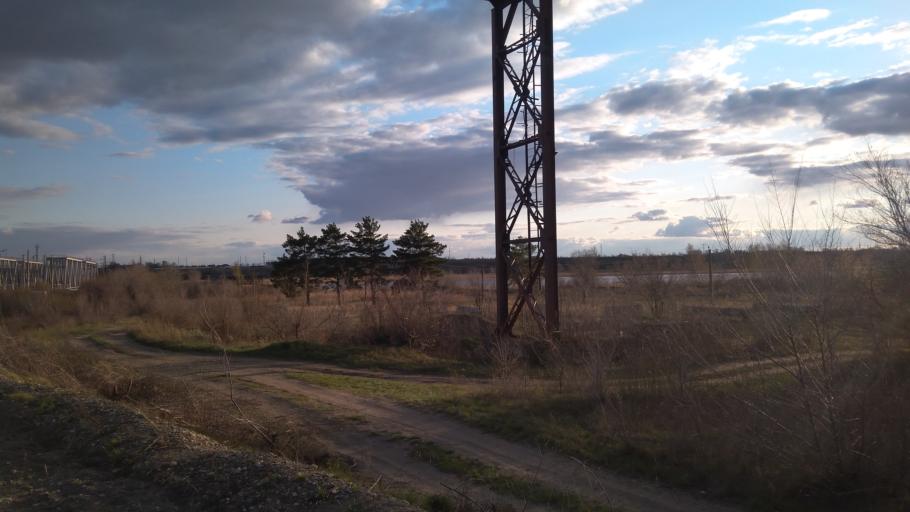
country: RU
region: Chelyabinsk
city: Troitsk
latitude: 54.0584
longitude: 61.6134
